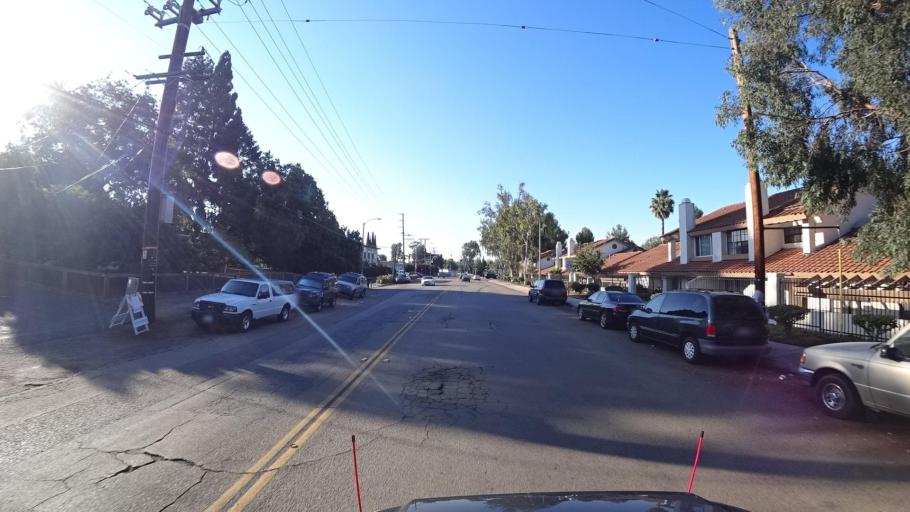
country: US
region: California
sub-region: San Diego County
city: Escondido
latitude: 33.1080
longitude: -117.0691
